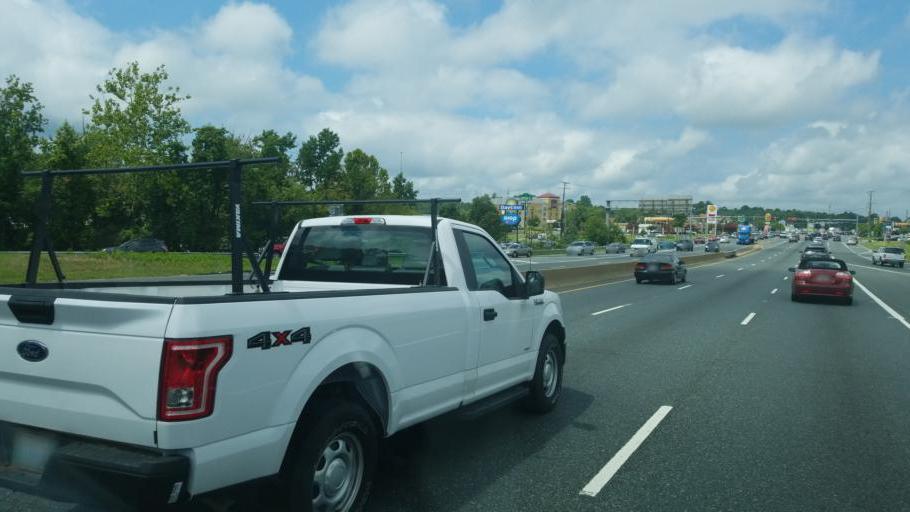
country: US
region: Virginia
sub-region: Stafford County
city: Falmouth
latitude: 38.3419
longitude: -77.4939
